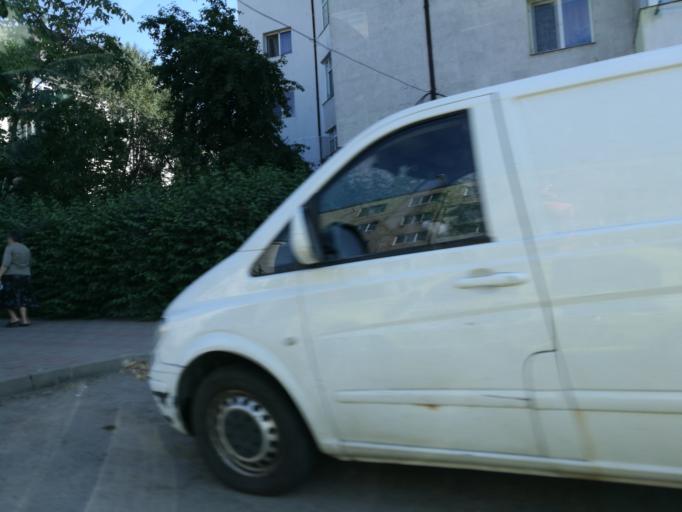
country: RO
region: Iasi
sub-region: Comuna Miroslava
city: Miroslava
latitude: 47.1731
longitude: 27.5429
